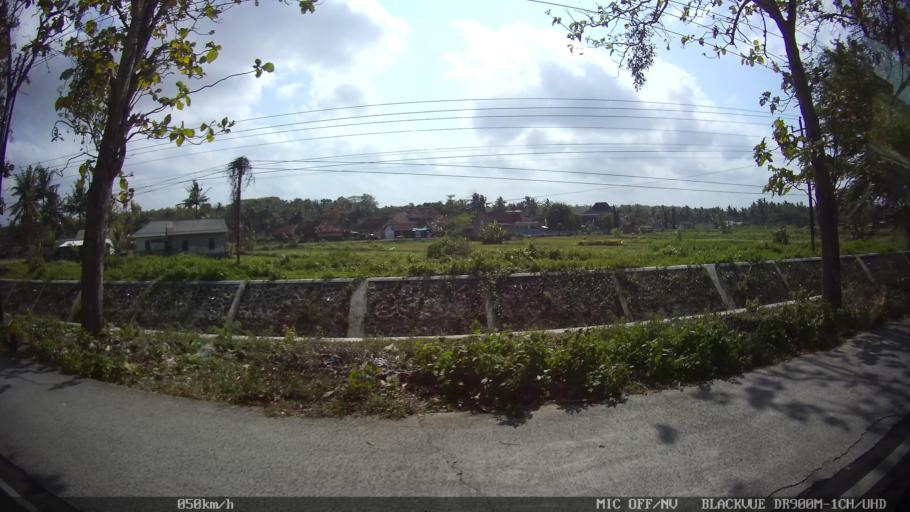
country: ID
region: Daerah Istimewa Yogyakarta
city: Srandakan
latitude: -7.8982
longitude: 110.1640
